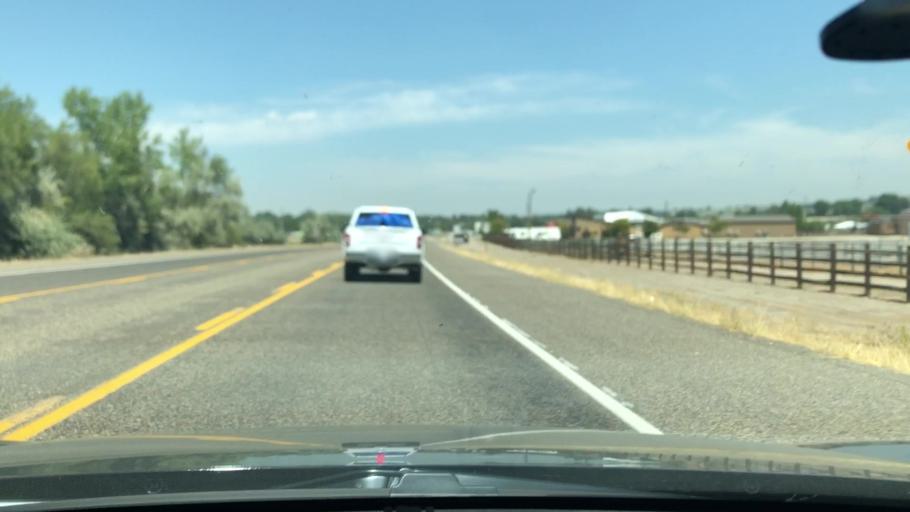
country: US
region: Idaho
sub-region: Owyhee County
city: Homedale
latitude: 43.6121
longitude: -116.9293
